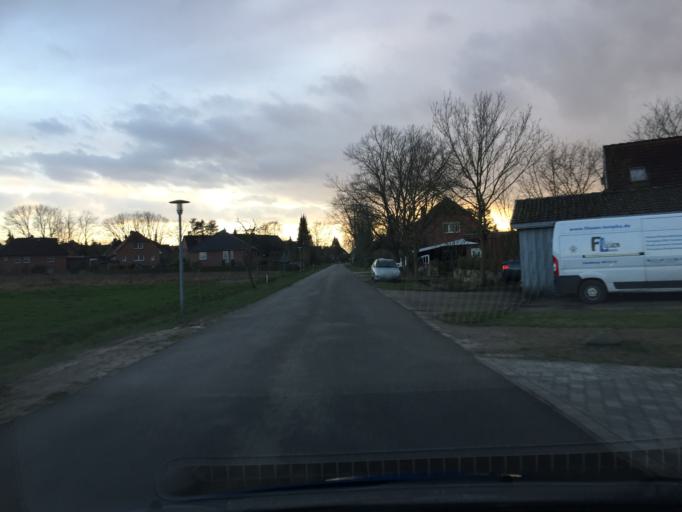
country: DE
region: Lower Saxony
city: Rullstorf
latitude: 53.2888
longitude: 10.5390
